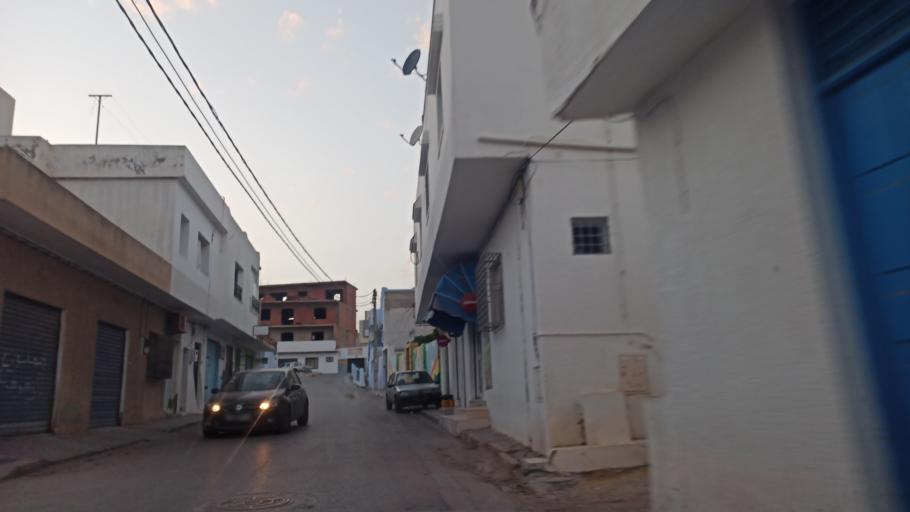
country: TN
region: Nabul
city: Al Hammamat
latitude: 36.4057
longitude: 10.6196
